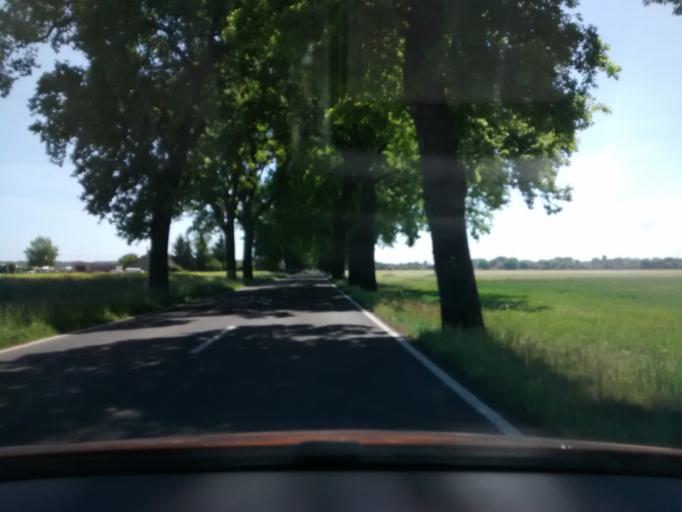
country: DE
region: Brandenburg
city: Storkow
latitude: 52.2701
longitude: 13.9220
